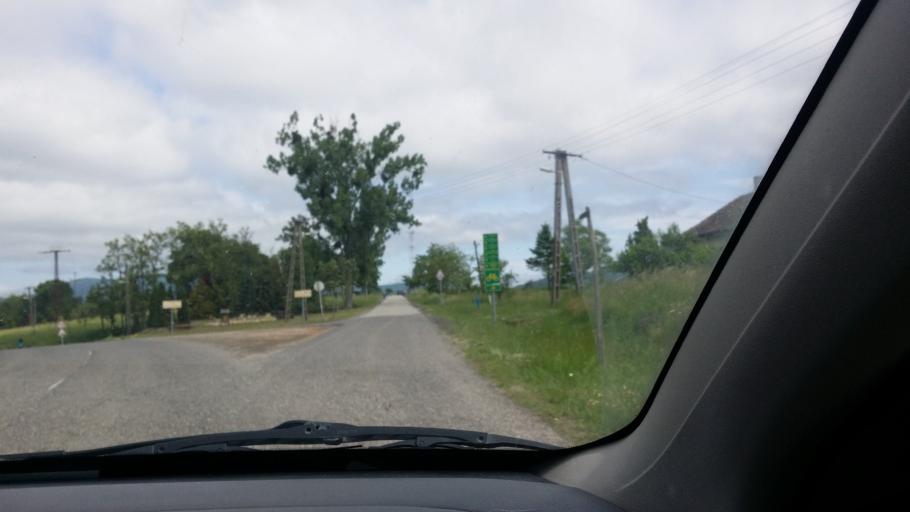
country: HU
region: Borsod-Abauj-Zemplen
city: Sarospatak
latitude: 48.4923
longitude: 21.4929
